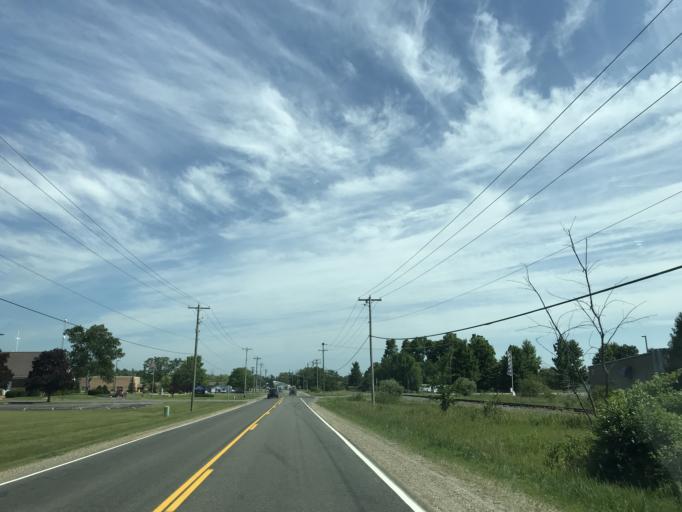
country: US
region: Michigan
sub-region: Grand Traverse County
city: Traverse City
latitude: 44.7135
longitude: -85.6265
